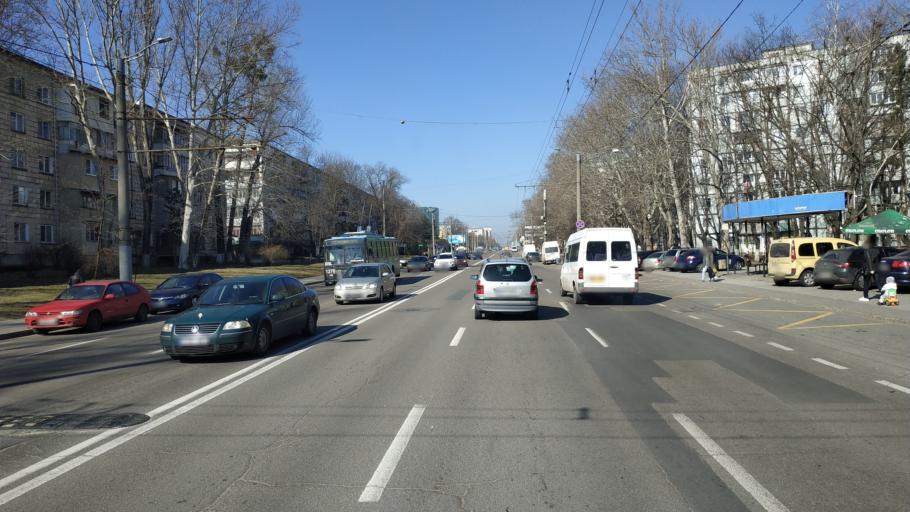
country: MD
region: Chisinau
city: Chisinau
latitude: 47.0278
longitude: 28.7914
